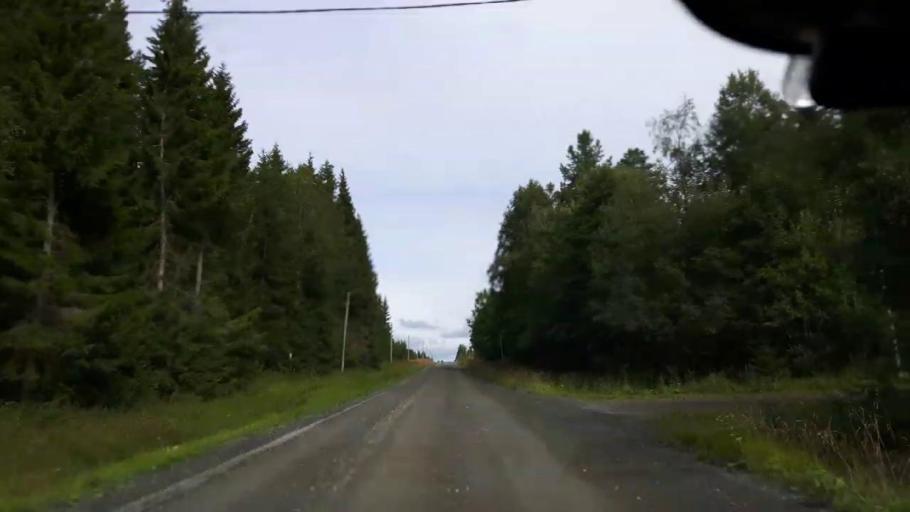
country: SE
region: Jaemtland
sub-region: Krokoms Kommun
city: Krokom
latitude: 63.3628
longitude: 14.1290
